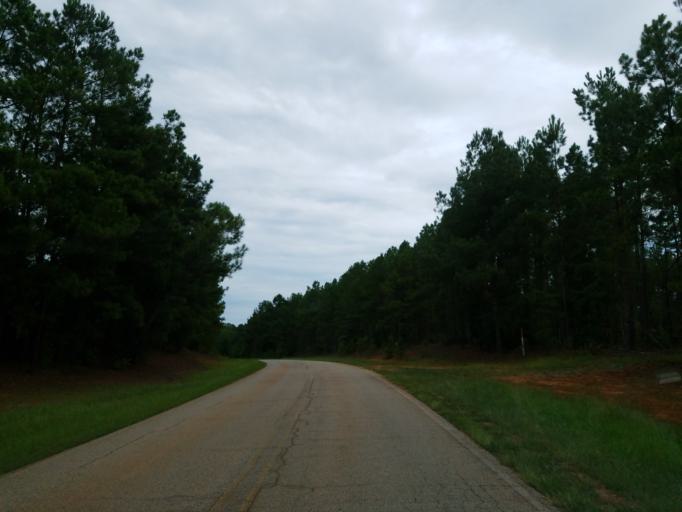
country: US
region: Georgia
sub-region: Monroe County
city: Forsyth
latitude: 32.9597
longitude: -83.9649
